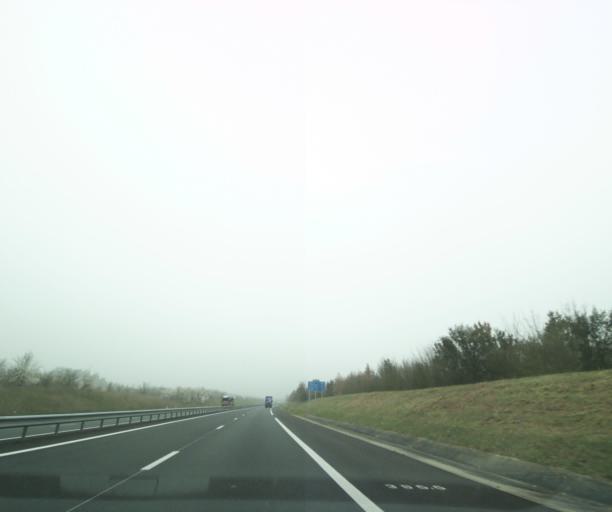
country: FR
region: Midi-Pyrenees
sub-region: Departement du Tarn-et-Garonne
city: Caussade
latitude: 44.1621
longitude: 1.5204
